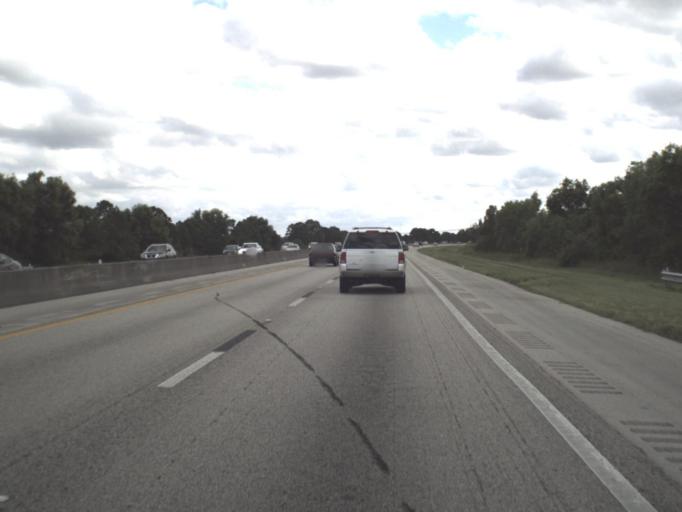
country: US
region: Florida
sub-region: Saint Lucie County
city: White City
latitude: 27.3599
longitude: -80.3769
